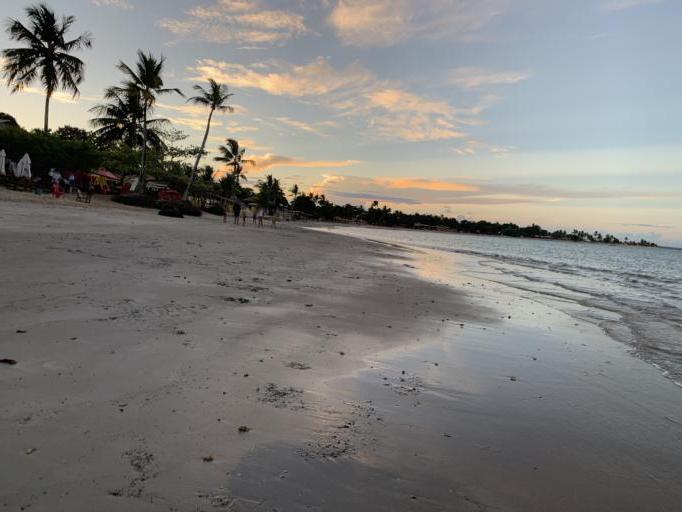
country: BR
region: Bahia
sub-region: Santa Cruz Cabralia
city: Santa Cruz Cabralia
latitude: -16.3411
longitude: -39.0063
